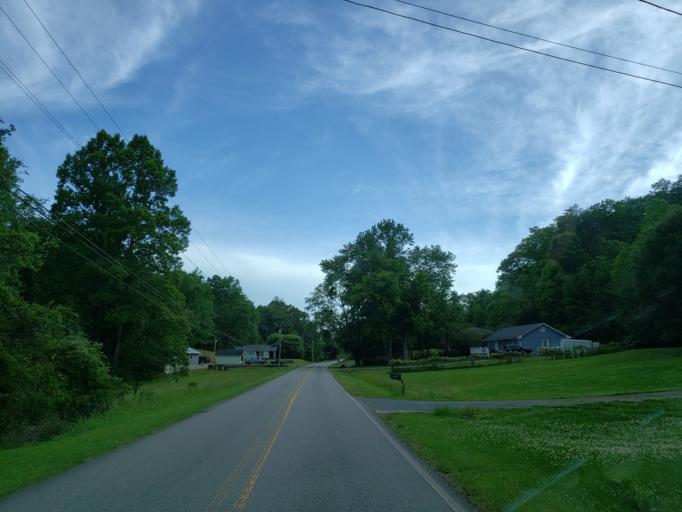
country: US
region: Georgia
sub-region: Fannin County
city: Blue Ridge
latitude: 34.8393
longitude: -84.3444
